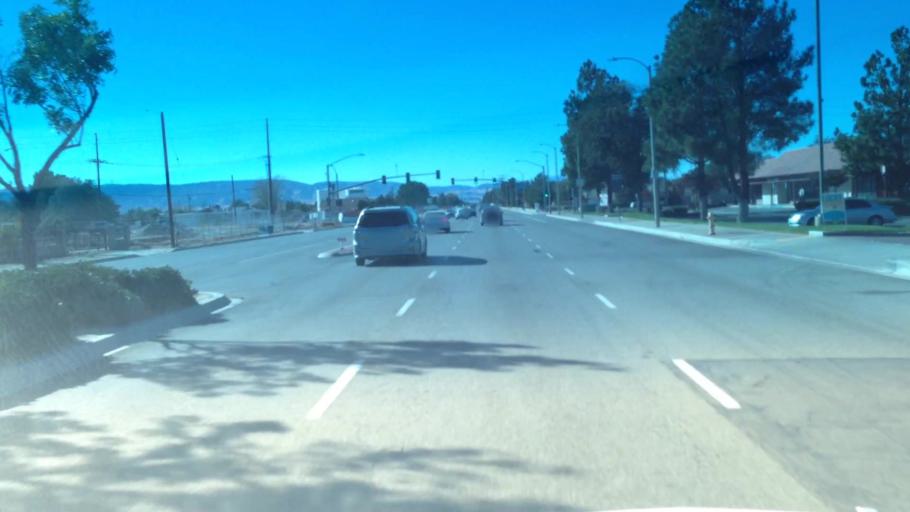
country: US
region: California
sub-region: Los Angeles County
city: Lancaster
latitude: 34.6605
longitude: -118.1638
